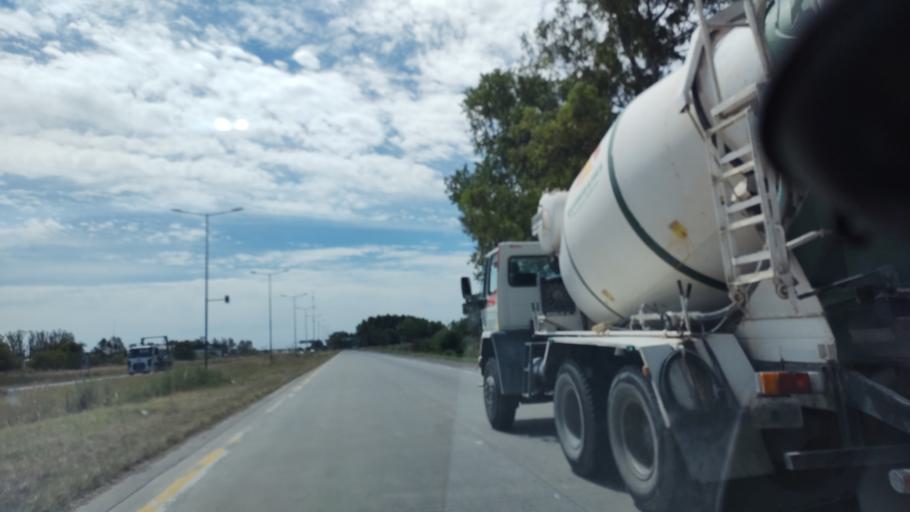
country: AR
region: Buenos Aires
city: Canuelas
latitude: -35.0358
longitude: -58.7188
